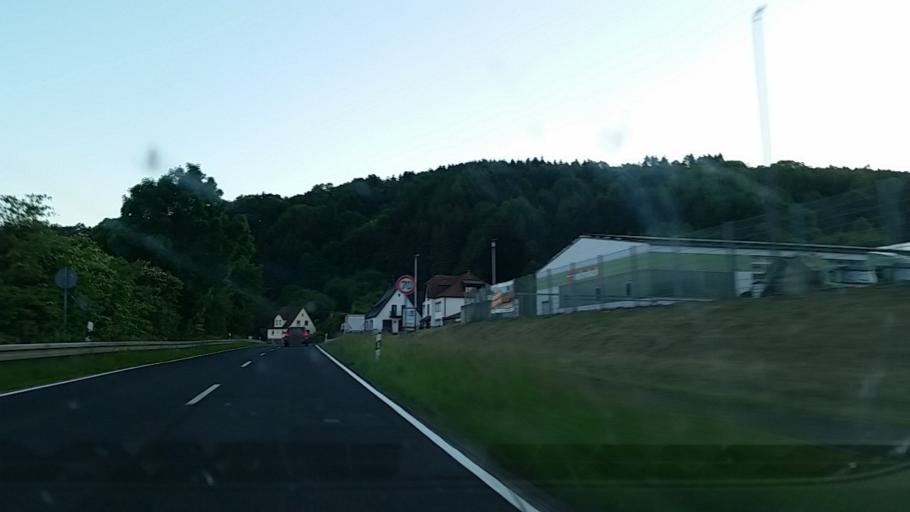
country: DE
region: Bavaria
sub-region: Regierungsbezirk Unterfranken
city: Rieneck
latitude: 50.0999
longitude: 9.6475
